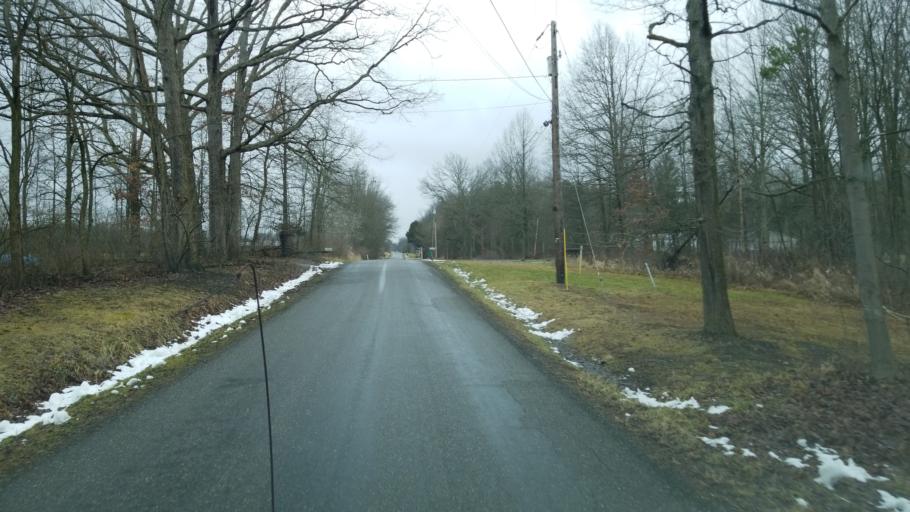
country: US
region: Ohio
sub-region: Trumbull County
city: Leavittsburg
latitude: 41.3393
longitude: -80.9633
